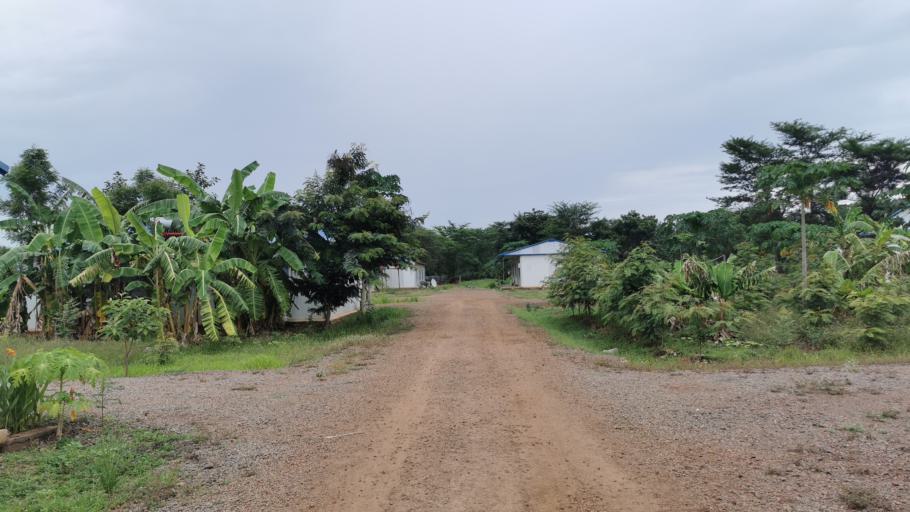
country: ET
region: Gambela
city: Gambela
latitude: 7.8859
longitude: 34.5099
